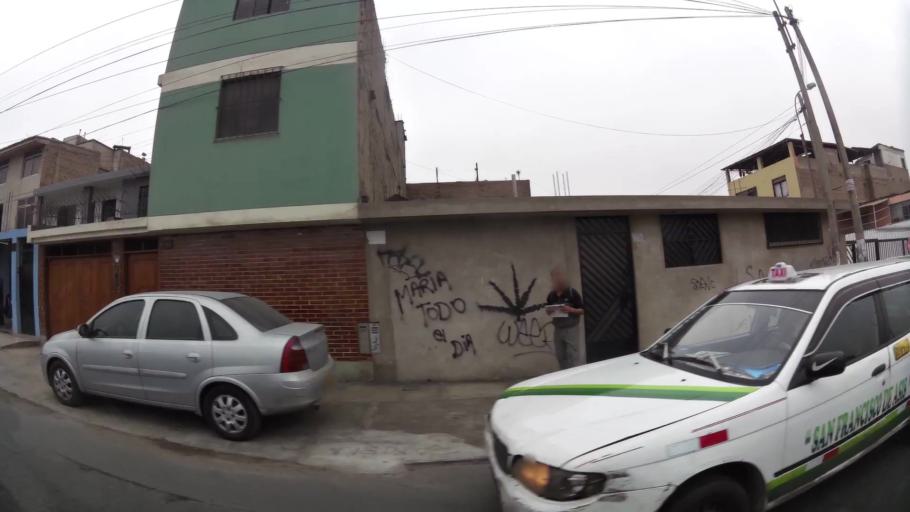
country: PE
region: Lima
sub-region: Lima
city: Surco
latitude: -12.1718
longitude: -76.9765
